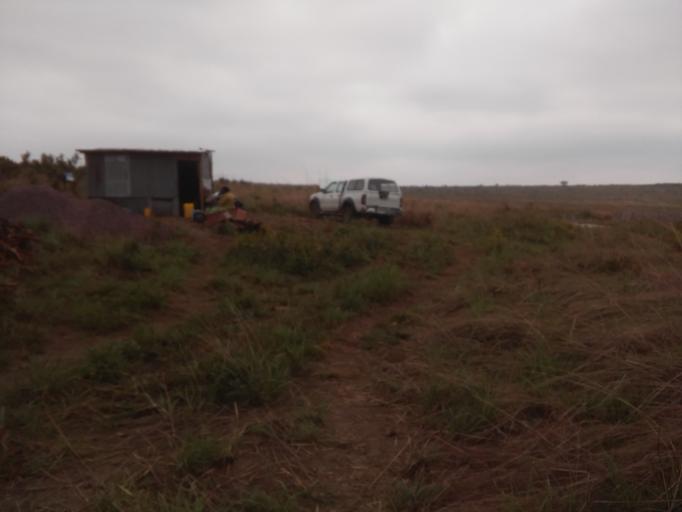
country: CD
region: Kinshasa
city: Masina
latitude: -4.4234
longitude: 15.9177
